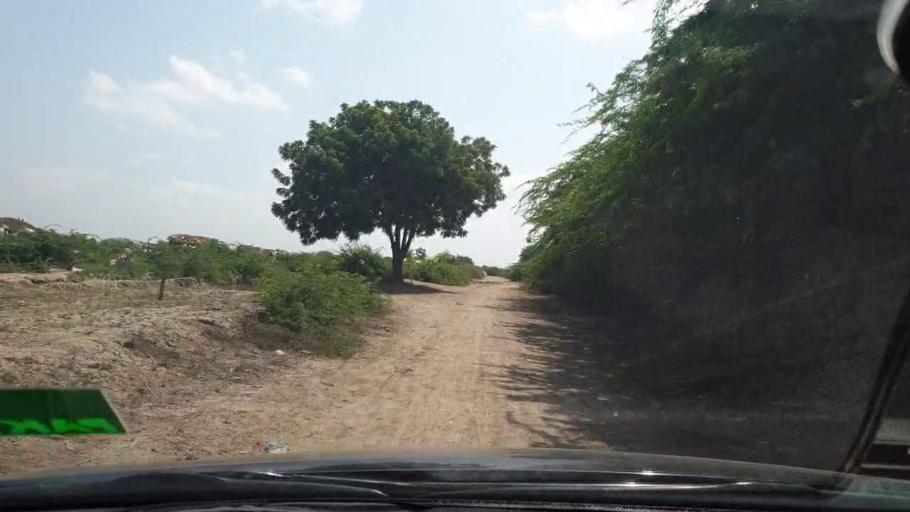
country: PK
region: Sindh
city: Tando Bago
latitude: 24.9339
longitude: 69.0658
